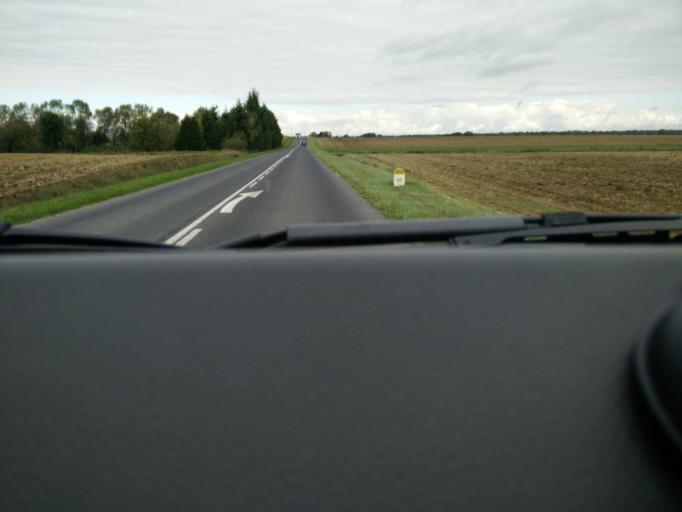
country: FR
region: Lorraine
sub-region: Departement de la Meuse
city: Vigneulles-les-Hattonchatel
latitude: 48.9755
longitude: 5.7954
